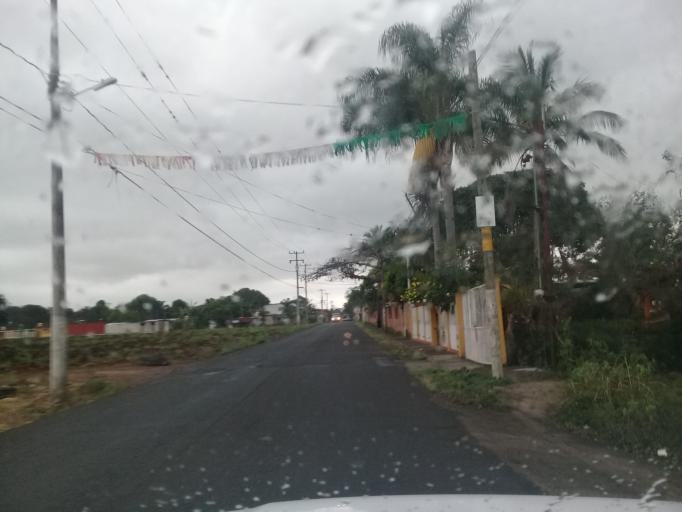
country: MX
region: Veracruz
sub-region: Cordoba
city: Veinte de Noviembre
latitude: 18.8609
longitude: -96.9525
